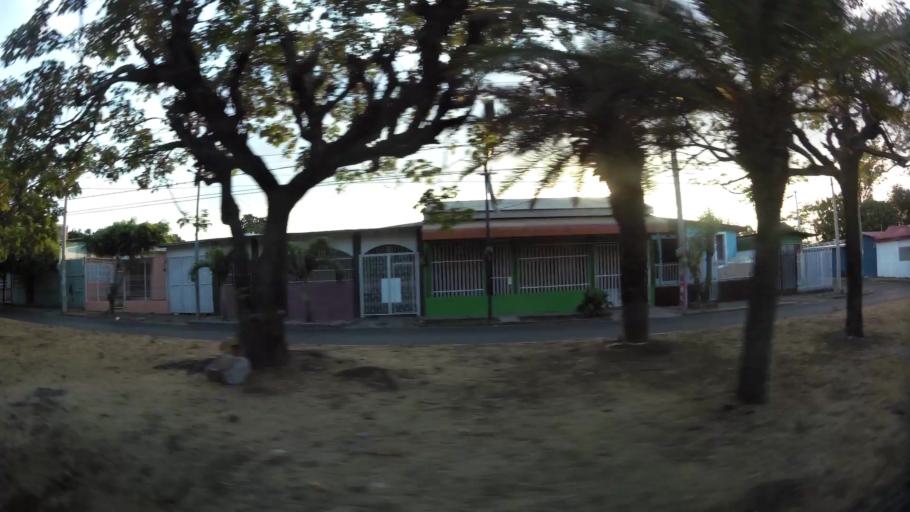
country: NI
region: Managua
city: Managua
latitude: 12.1396
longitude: -86.2333
